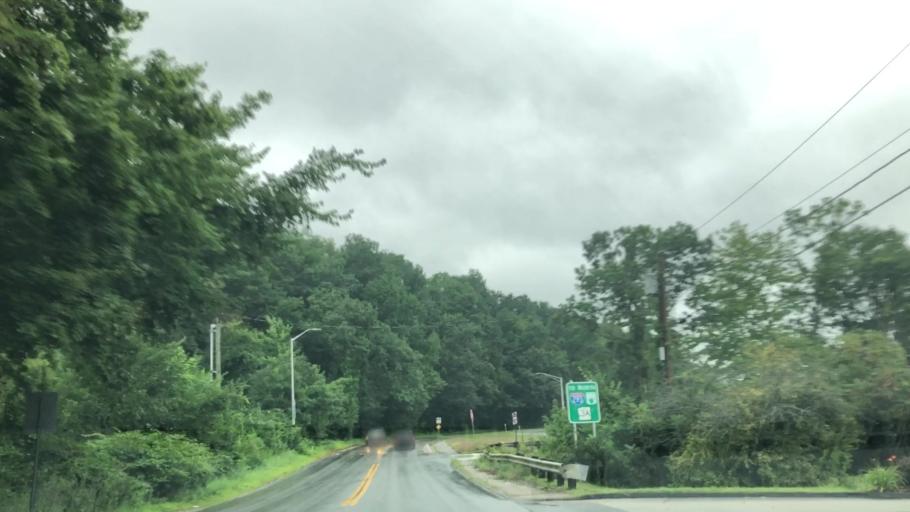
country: US
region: New Hampshire
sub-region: Hillsborough County
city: Manchester
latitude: 43.0002
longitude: -71.4760
